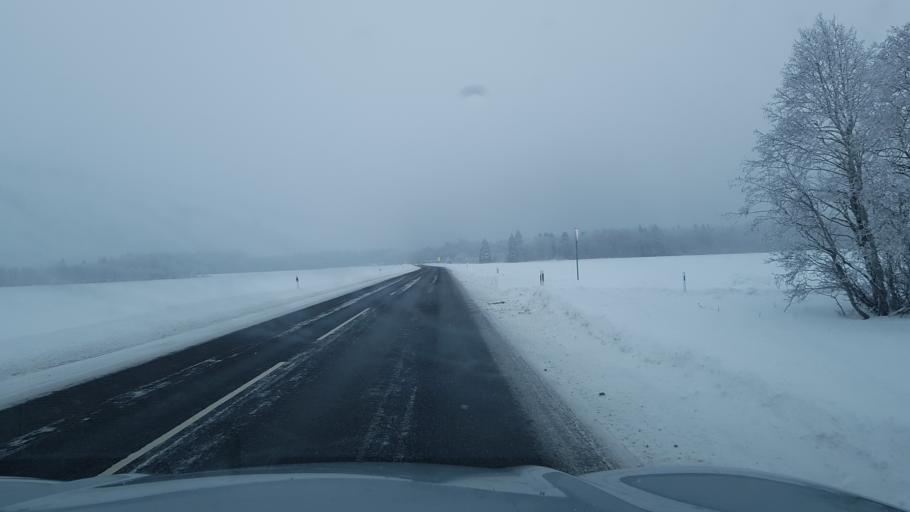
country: EE
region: Ida-Virumaa
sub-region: Johvi vald
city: Johvi
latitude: 59.3156
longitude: 27.3925
